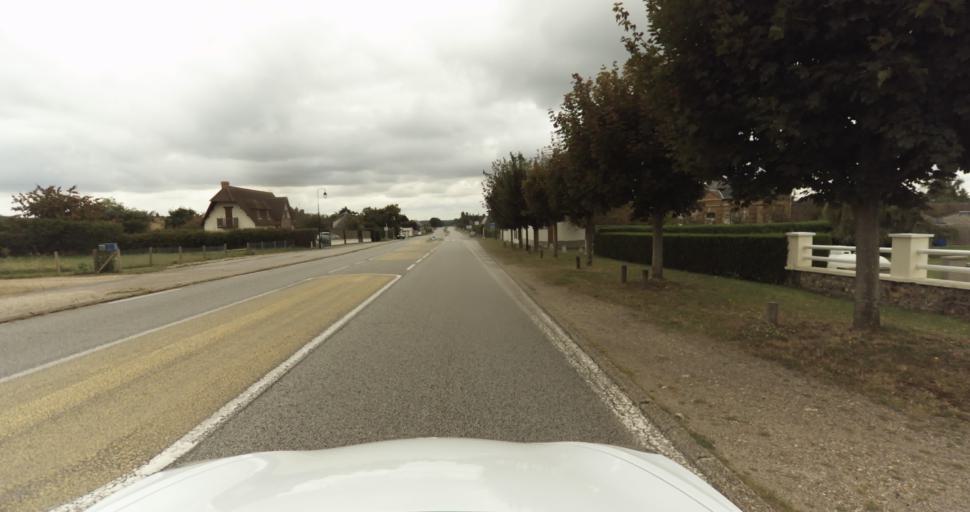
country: FR
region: Haute-Normandie
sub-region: Departement de l'Eure
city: Saint-Sebastien-de-Morsent
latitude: 49.0337
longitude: 1.0968
